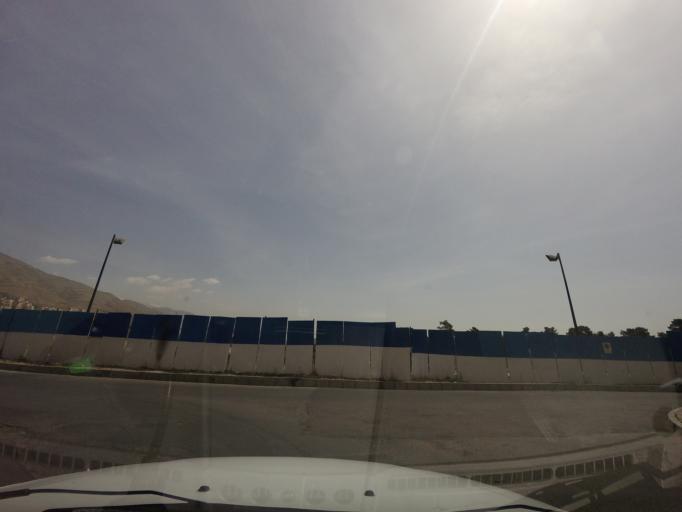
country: IR
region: Tehran
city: Shahr-e Qods
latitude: 35.7461
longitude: 51.1986
